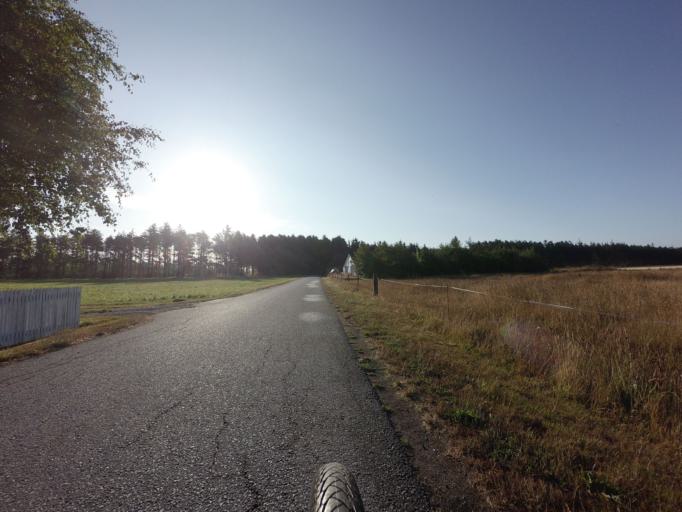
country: DK
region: North Denmark
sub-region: Hjorring Kommune
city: Vra
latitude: 57.3623
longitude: 9.8810
